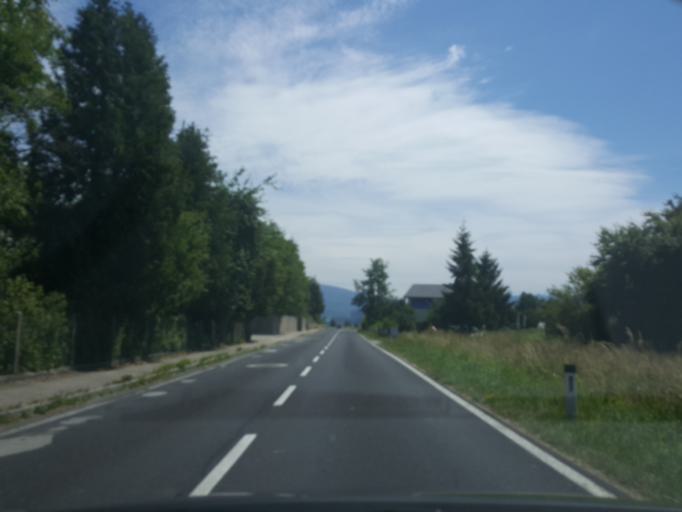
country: AT
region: Upper Austria
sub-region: Politischer Bezirk Vocklabruck
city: Seewalchen
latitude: 47.9604
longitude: 13.5739
